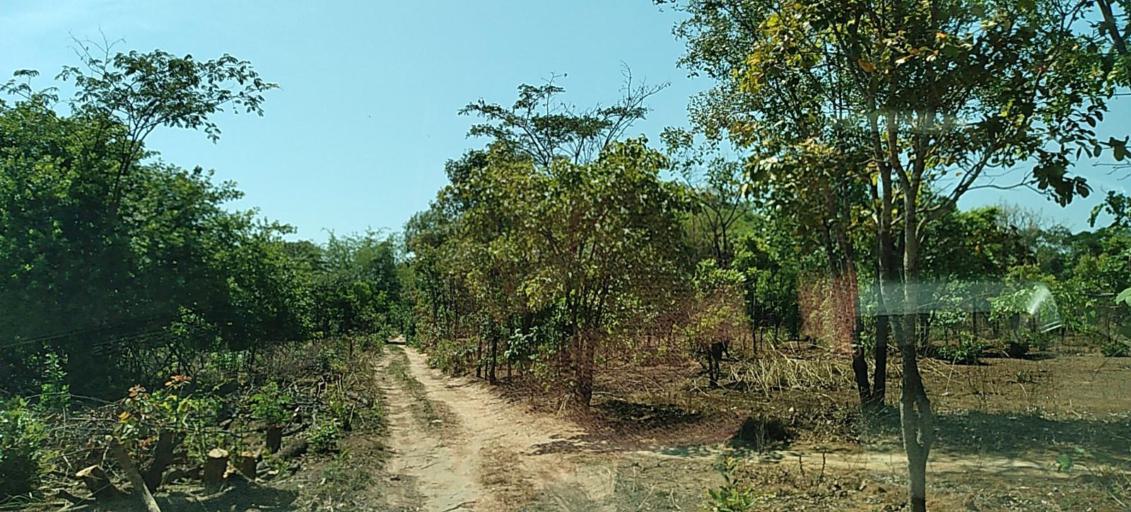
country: ZM
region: Copperbelt
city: Chililabombwe
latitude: -12.2891
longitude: 27.8903
